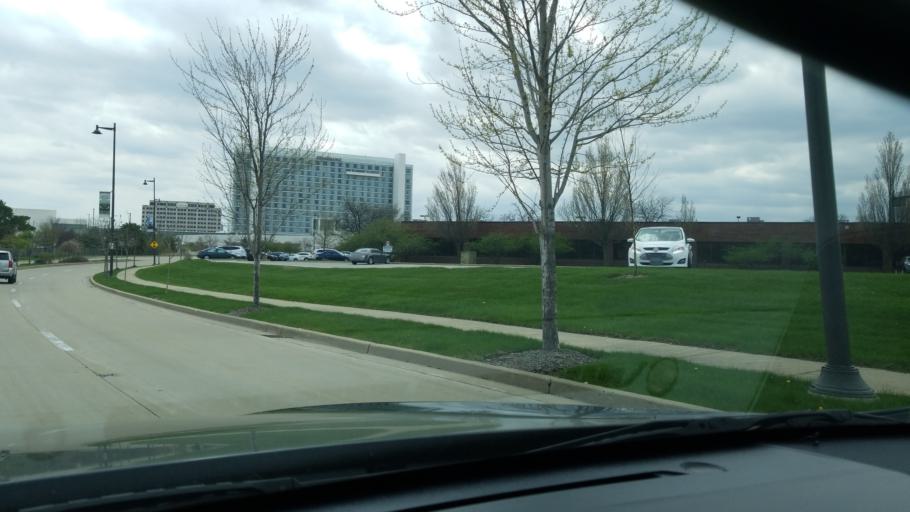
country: US
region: Illinois
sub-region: Cook County
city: Rolling Meadows
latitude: 42.0643
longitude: -88.0404
